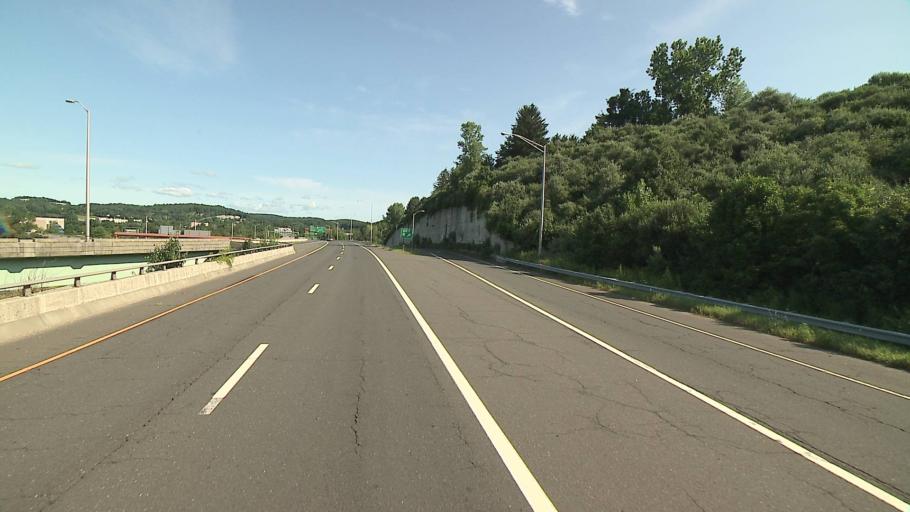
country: US
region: Connecticut
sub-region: Fairfield County
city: Danbury
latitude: 41.3775
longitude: -73.4733
